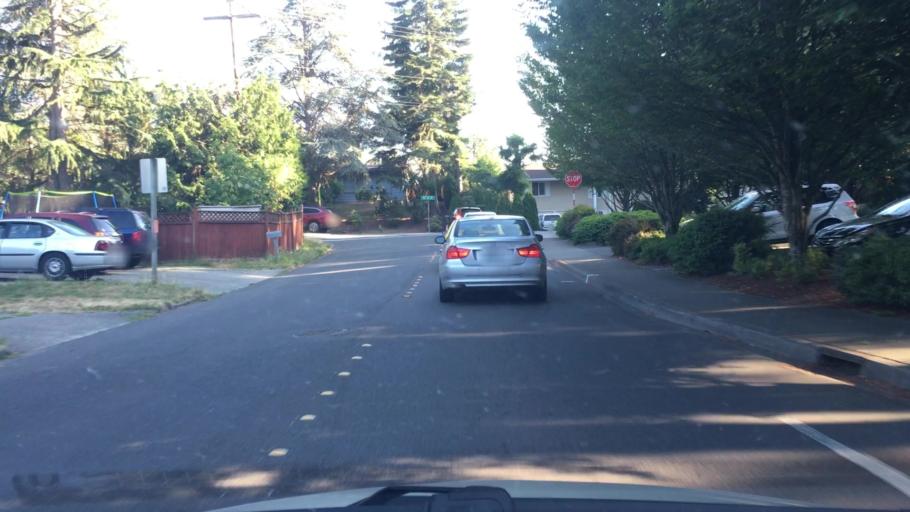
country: US
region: Washington
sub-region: King County
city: West Lake Sammamish
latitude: 47.5986
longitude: -122.1211
